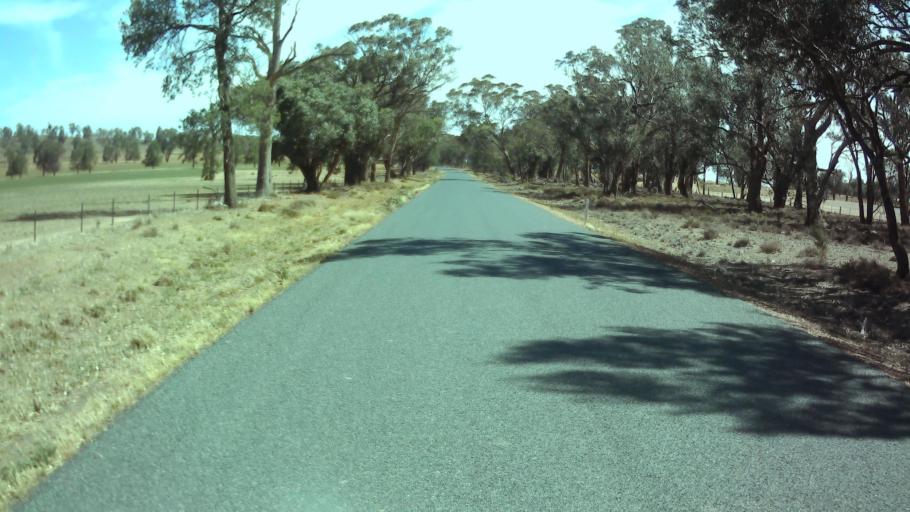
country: AU
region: New South Wales
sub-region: Weddin
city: Grenfell
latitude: -34.0445
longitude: 148.1322
